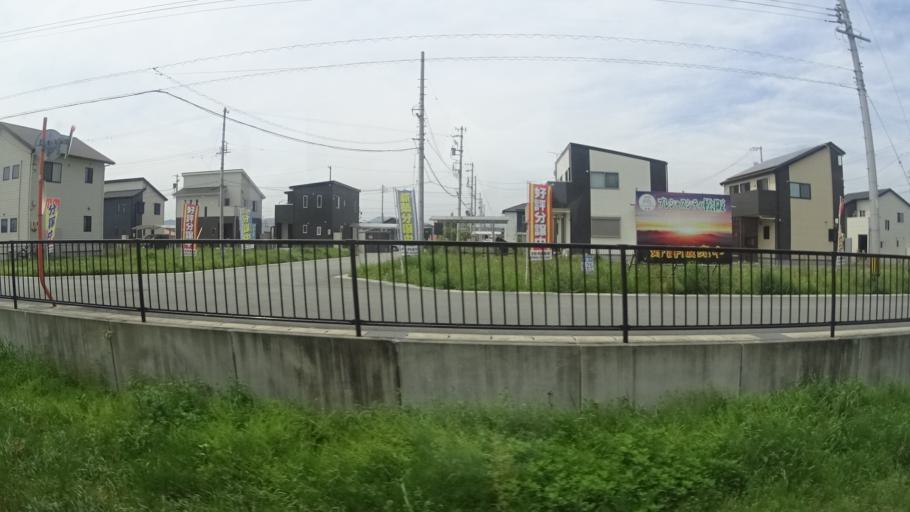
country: JP
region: Mie
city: Hisai-motomachi
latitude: 34.5692
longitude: 136.5428
